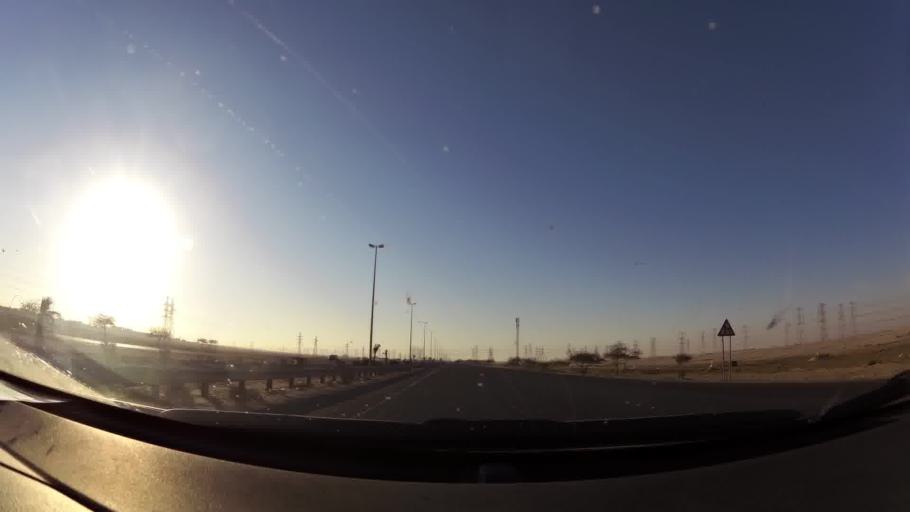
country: KW
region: Al Ahmadi
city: Al Fahahil
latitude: 28.7722
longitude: 48.2770
